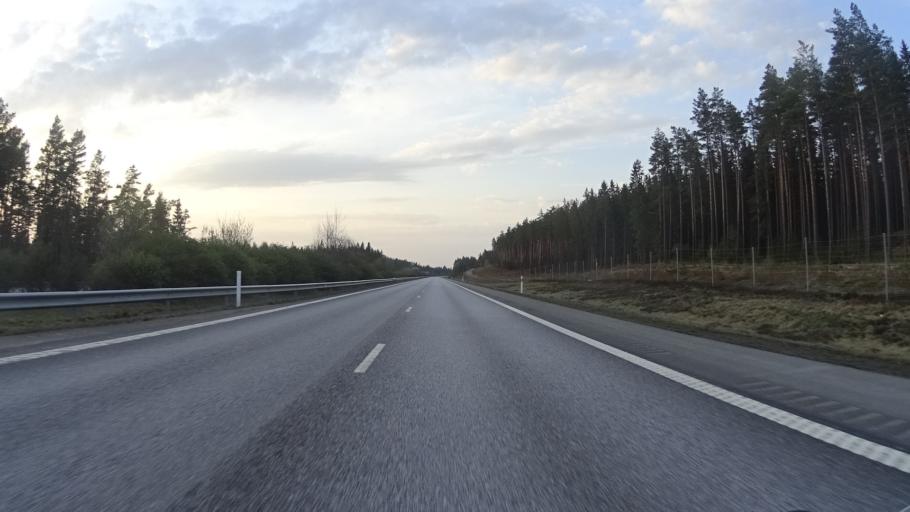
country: SE
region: Joenkoeping
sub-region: Varnamo Kommun
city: Varnamo
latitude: 57.2229
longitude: 14.0812
